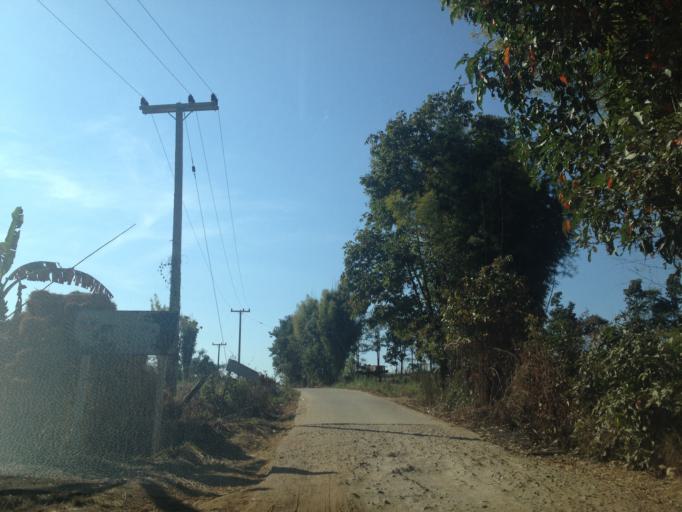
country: TH
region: Mae Hong Son
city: Ban Huai I Huak
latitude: 18.0738
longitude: 98.1863
